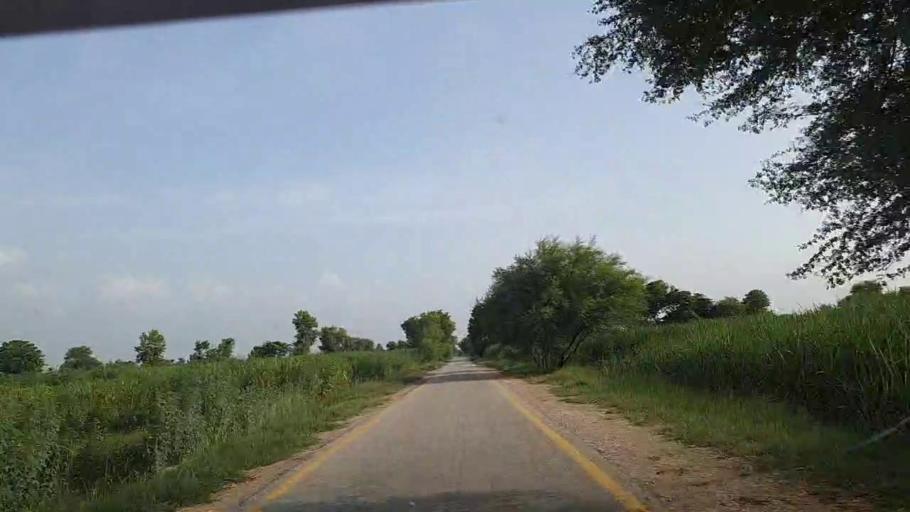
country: PK
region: Sindh
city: Adilpur
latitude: 27.9690
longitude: 69.2560
